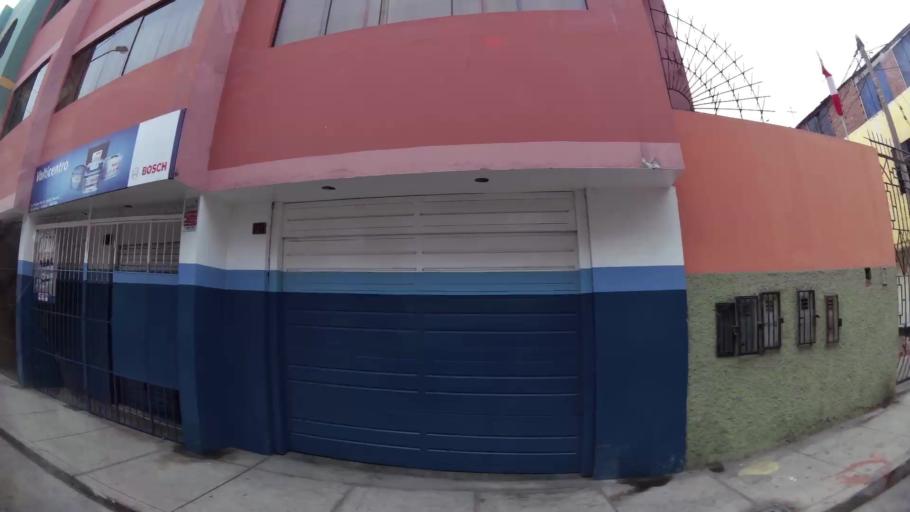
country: PE
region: Lima
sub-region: Lima
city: Surco
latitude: -12.1486
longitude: -77.0182
